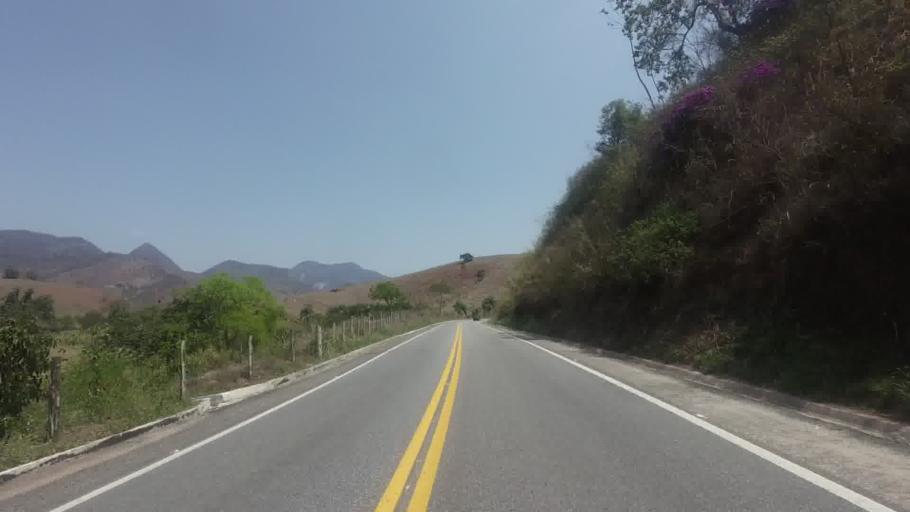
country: BR
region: Espirito Santo
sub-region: Mimoso Do Sul
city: Mimoso do Sul
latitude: -20.9222
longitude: -41.3117
